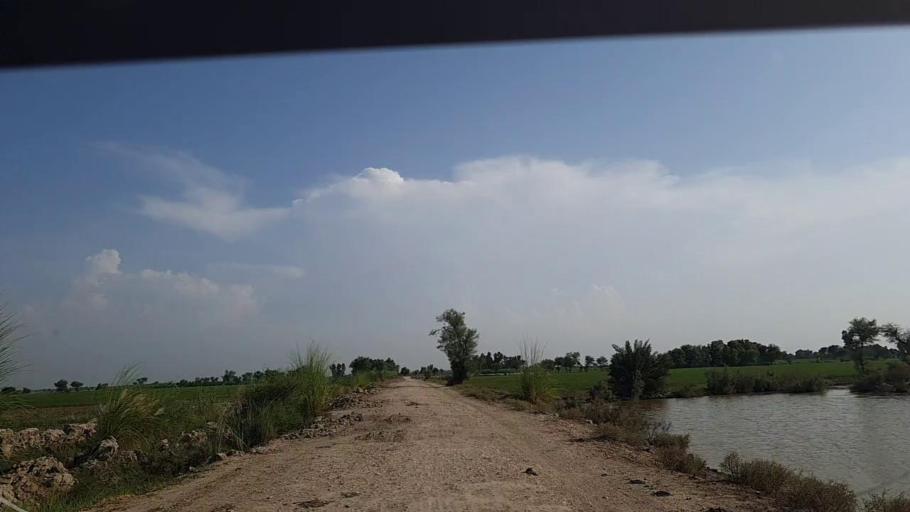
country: PK
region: Sindh
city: Khanpur
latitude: 27.8685
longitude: 69.3752
